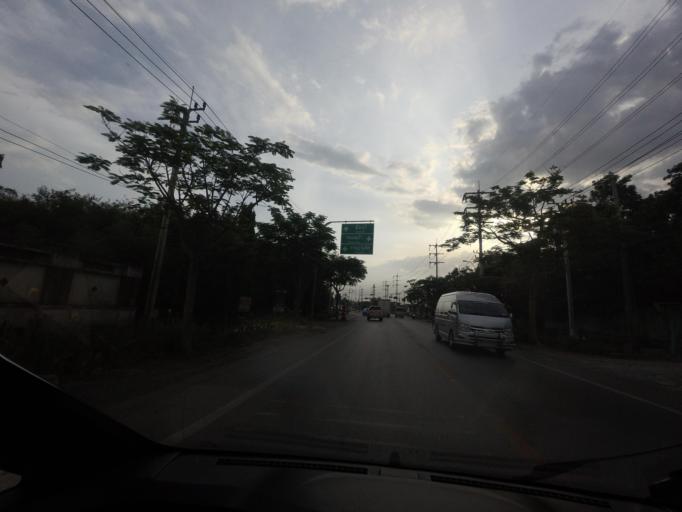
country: TH
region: Bangkok
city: Nong Chok
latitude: 13.8545
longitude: 100.8084
